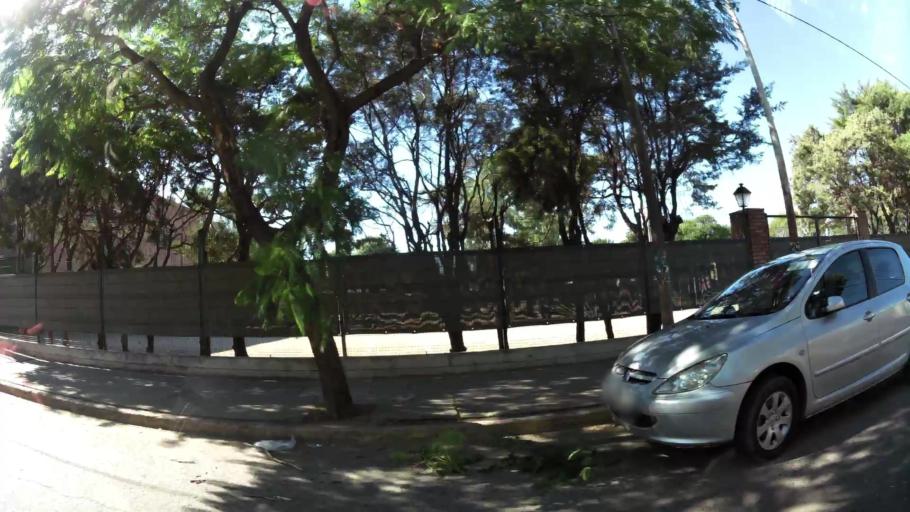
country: AR
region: Cordoba
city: Villa Allende
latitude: -31.3515
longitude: -64.2484
